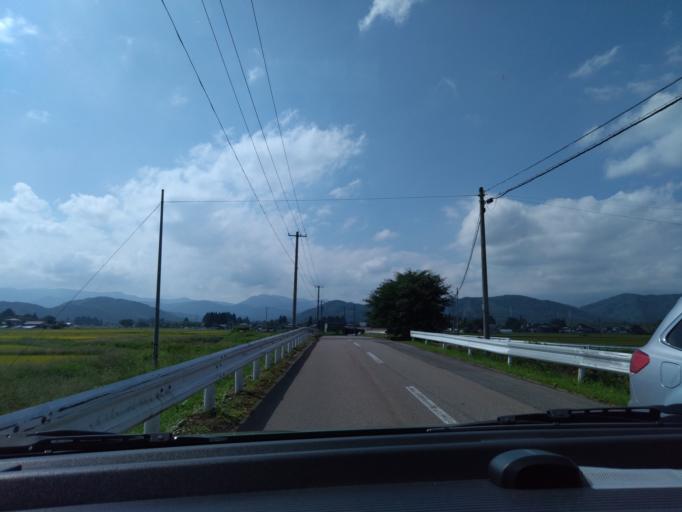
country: JP
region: Iwate
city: Shizukuishi
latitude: 39.6855
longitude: 140.9511
